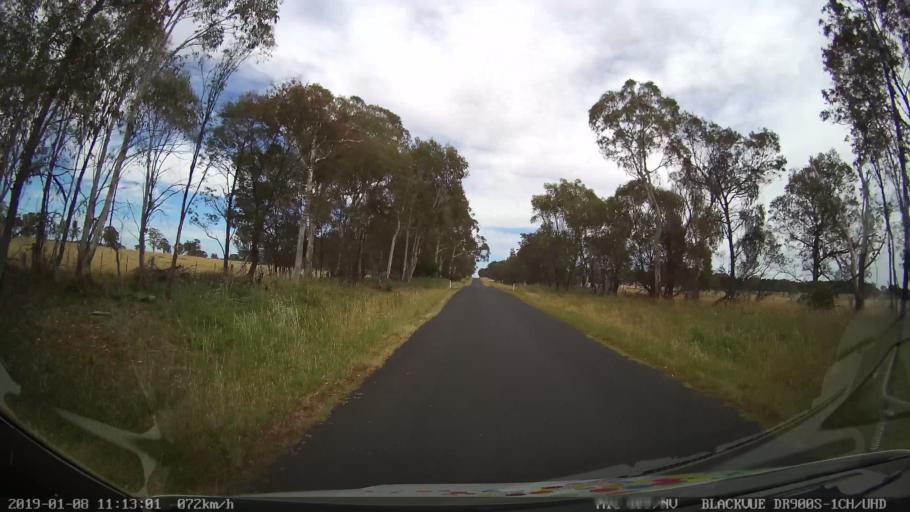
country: AU
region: New South Wales
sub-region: Guyra
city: Guyra
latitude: -30.2306
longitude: 151.6061
